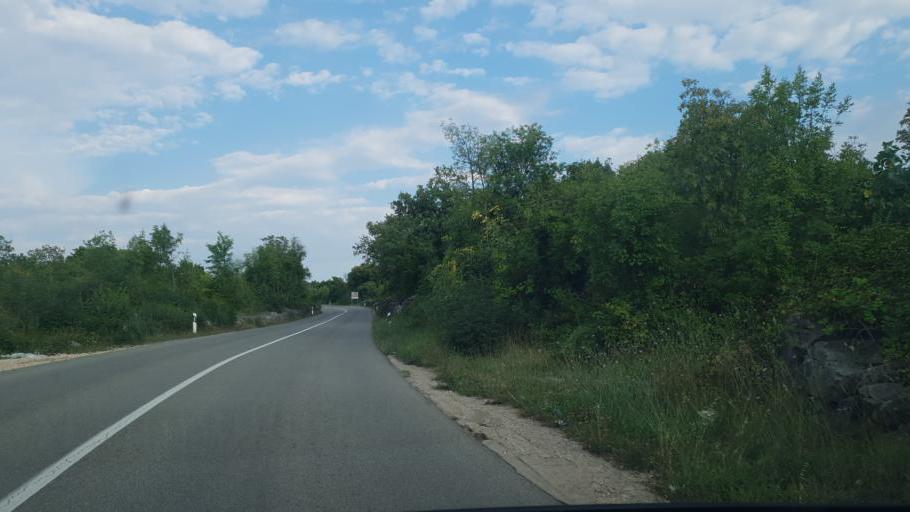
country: HR
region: Primorsko-Goranska
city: Njivice
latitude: 45.1219
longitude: 14.5518
